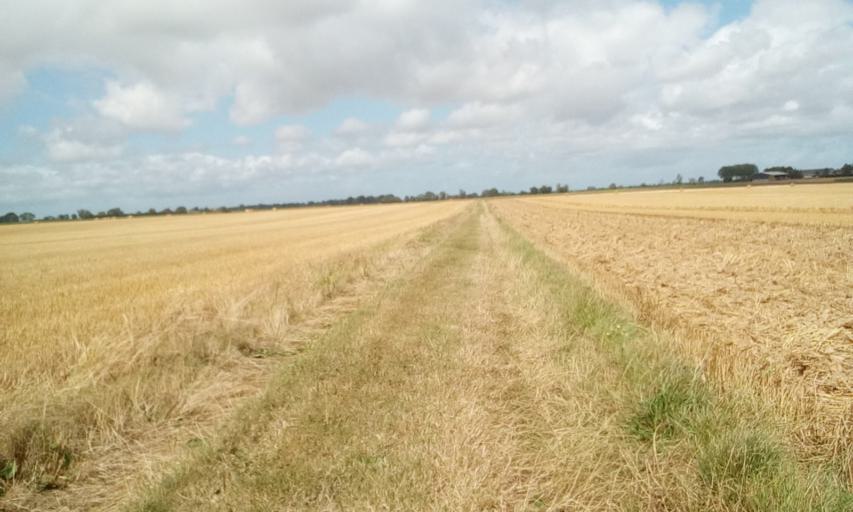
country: FR
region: Lower Normandy
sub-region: Departement du Calvados
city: Cheux
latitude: 49.1840
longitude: -0.5567
